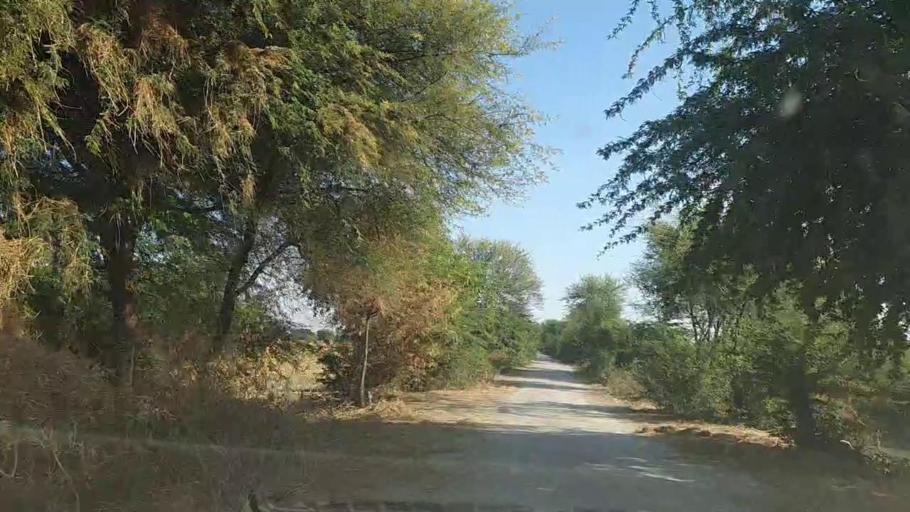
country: PK
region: Sindh
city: Bulri
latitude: 24.7917
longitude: 68.3444
